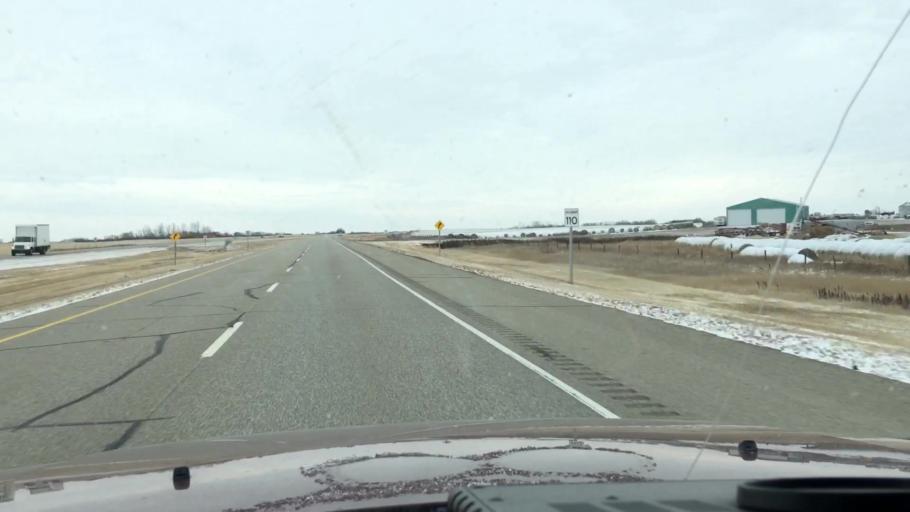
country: CA
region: Saskatchewan
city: Watrous
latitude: 51.3665
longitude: -106.1326
